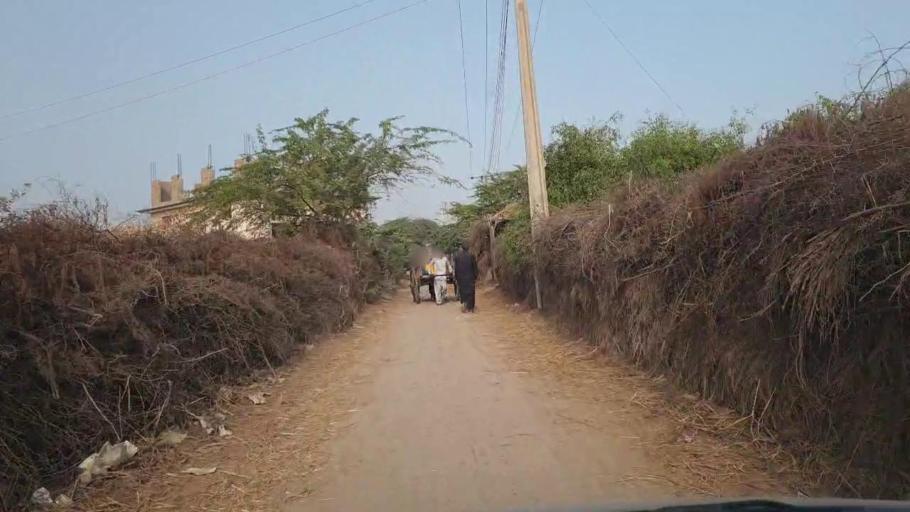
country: PK
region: Sindh
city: Matli
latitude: 25.0361
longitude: 68.7390
